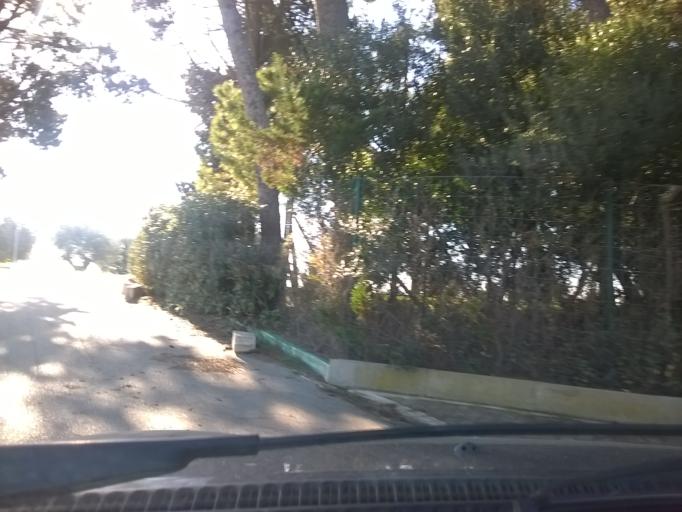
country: IT
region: Apulia
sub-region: Provincia di Taranto
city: Paolo VI
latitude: 40.4668
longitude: 17.3022
